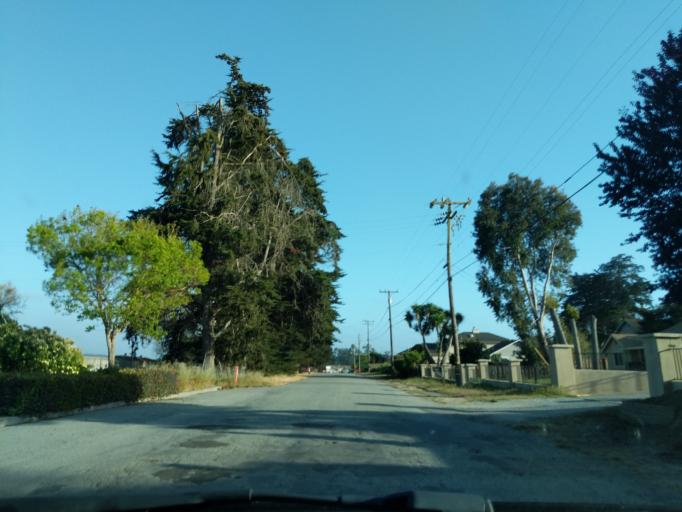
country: US
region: California
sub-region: Monterey County
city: Las Lomas
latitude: 36.8689
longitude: -121.7600
